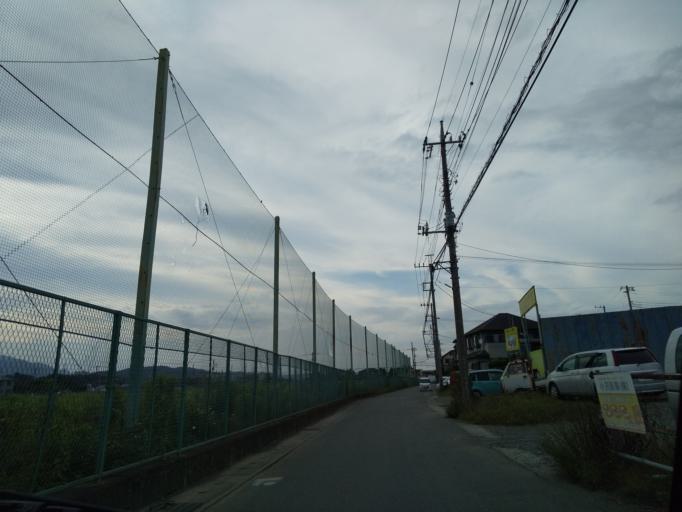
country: JP
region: Kanagawa
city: Zama
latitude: 35.4755
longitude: 139.3598
